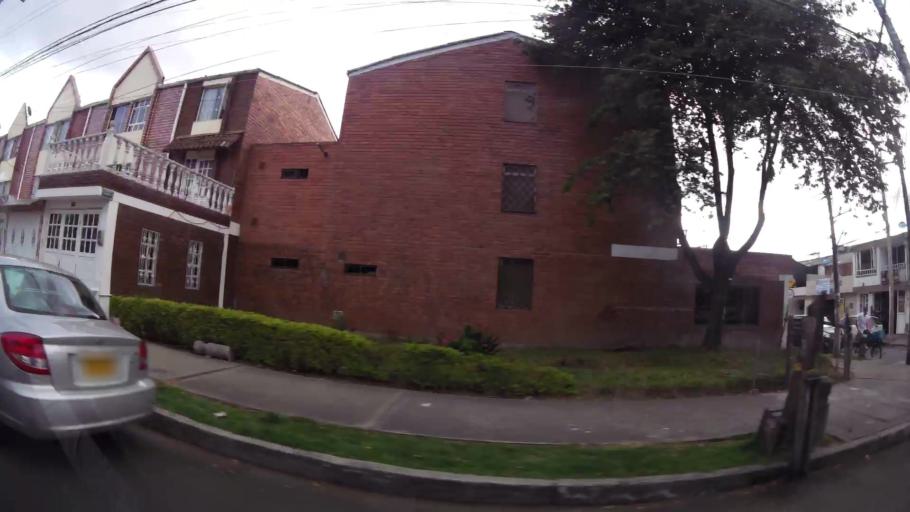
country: CO
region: Bogota D.C.
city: Bogota
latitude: 4.6092
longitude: -74.1208
